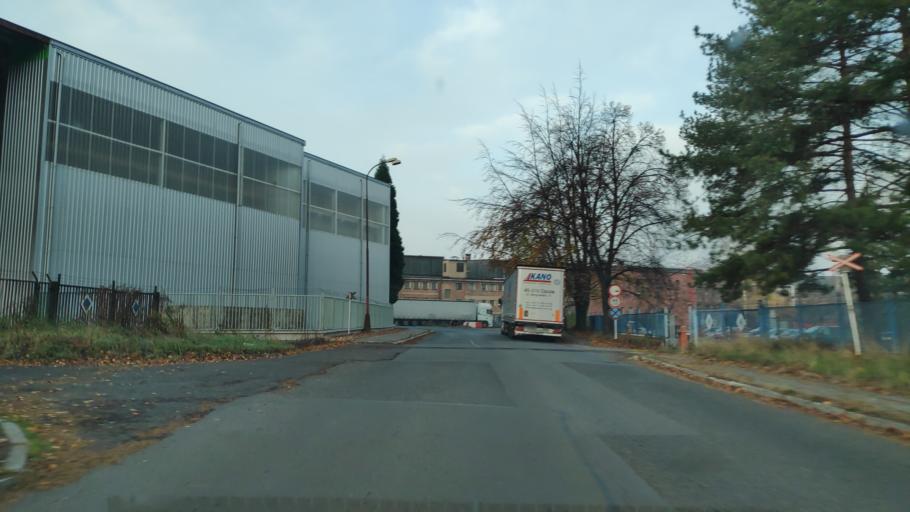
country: CZ
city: Sviadnov
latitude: 49.6948
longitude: 18.3347
